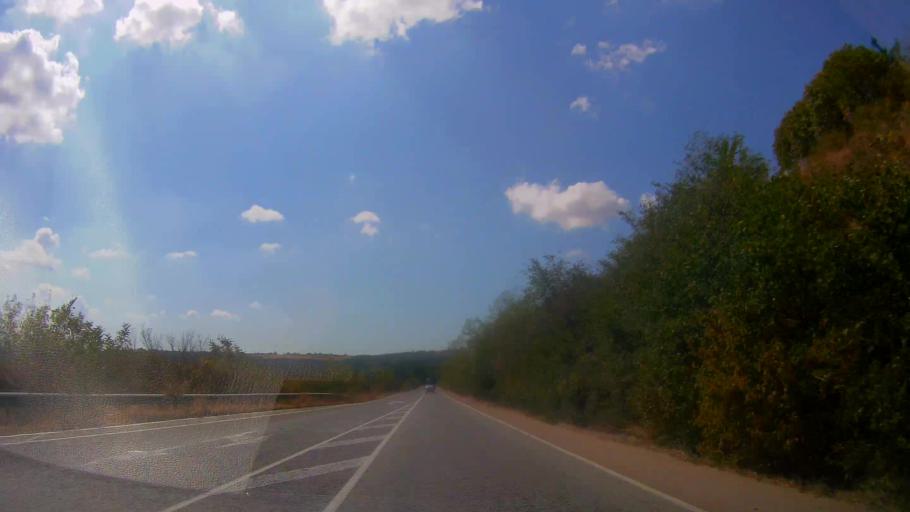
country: BG
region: Veliko Turnovo
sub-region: Obshtina Polski Trumbesh
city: Polski Trumbesh
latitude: 43.4463
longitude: 25.6573
